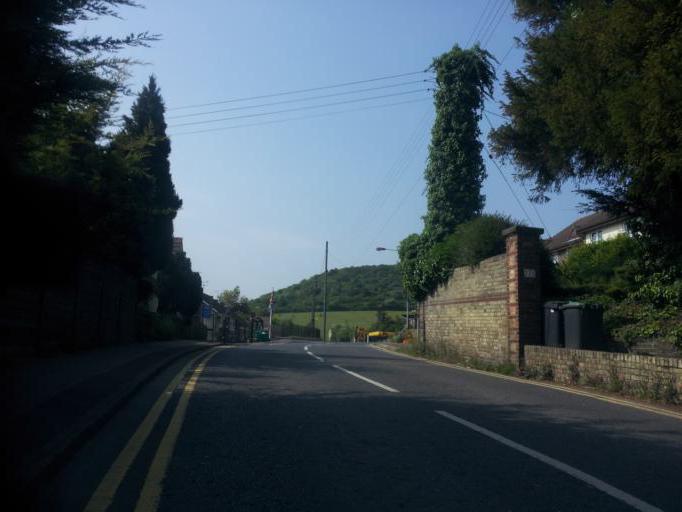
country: GB
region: England
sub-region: Kent
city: Aylesford
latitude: 51.3323
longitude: 0.4791
